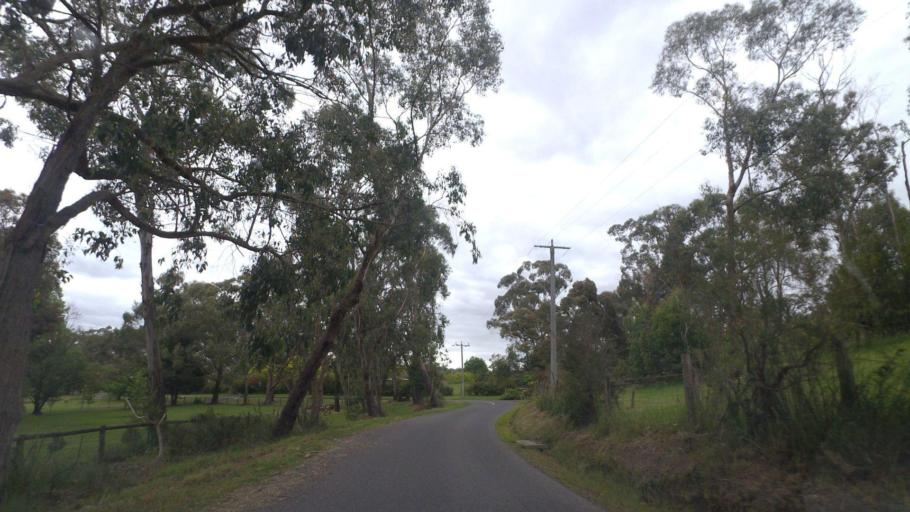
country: AU
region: Victoria
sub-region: Yarra Ranges
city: Mount Evelyn
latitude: -37.7587
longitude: 145.4219
